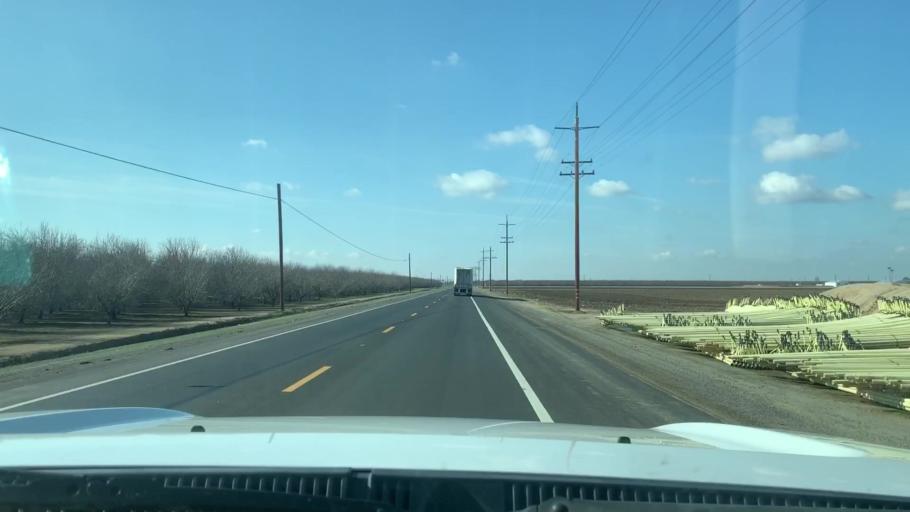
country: US
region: California
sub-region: Kern County
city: Wasco
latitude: 35.6017
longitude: -119.3044
